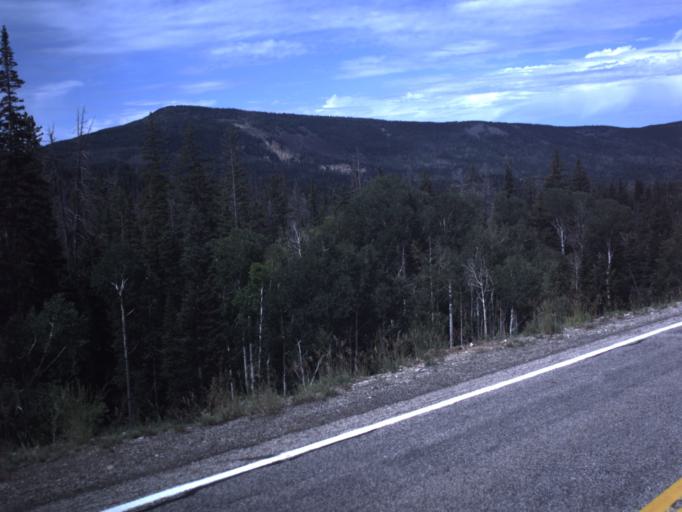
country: US
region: Utah
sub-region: Iron County
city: Cedar City
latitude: 37.5930
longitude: -112.8848
